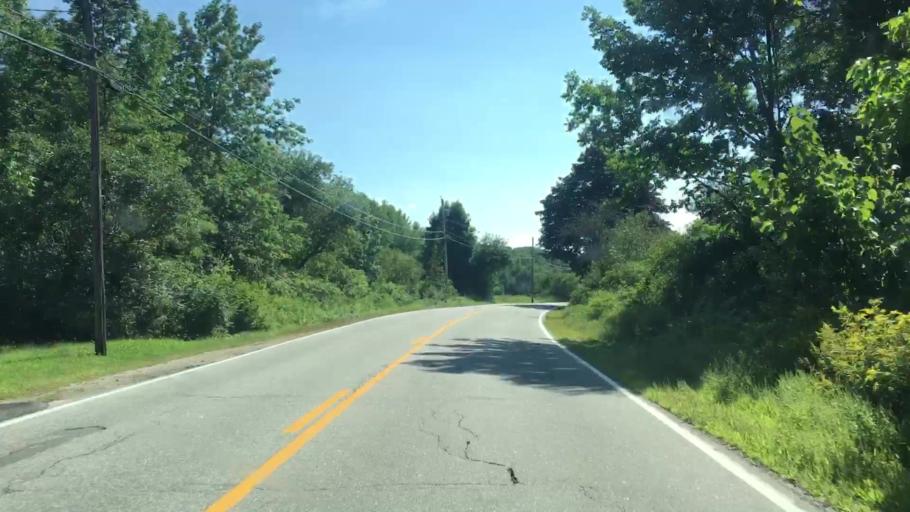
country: US
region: Maine
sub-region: Androscoggin County
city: Sabattus
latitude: 44.1511
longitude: -70.0818
